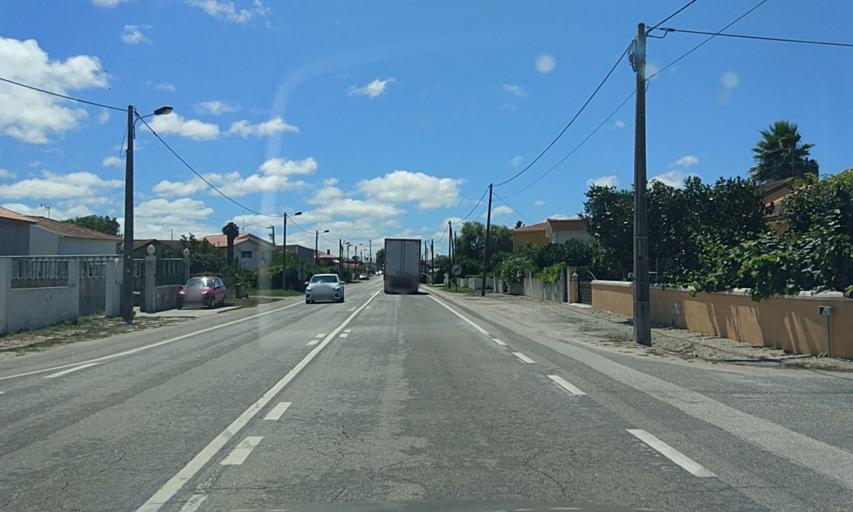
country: PT
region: Coimbra
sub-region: Mira
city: Mira
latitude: 40.4692
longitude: -8.6983
